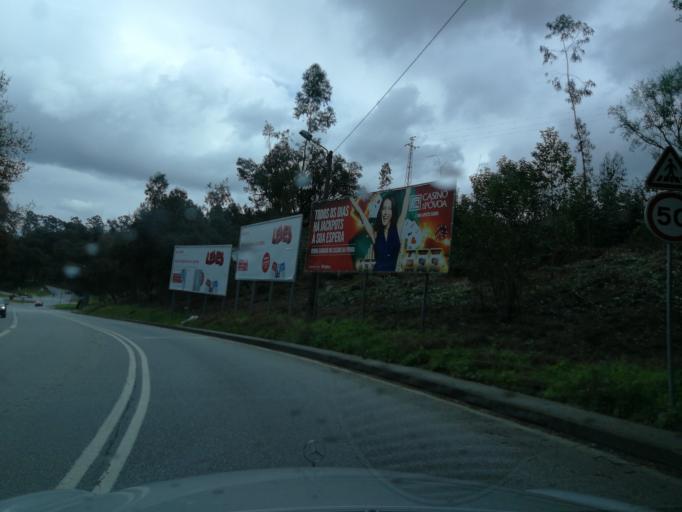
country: PT
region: Braga
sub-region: Braga
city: Braga
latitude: 41.5377
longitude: -8.4202
